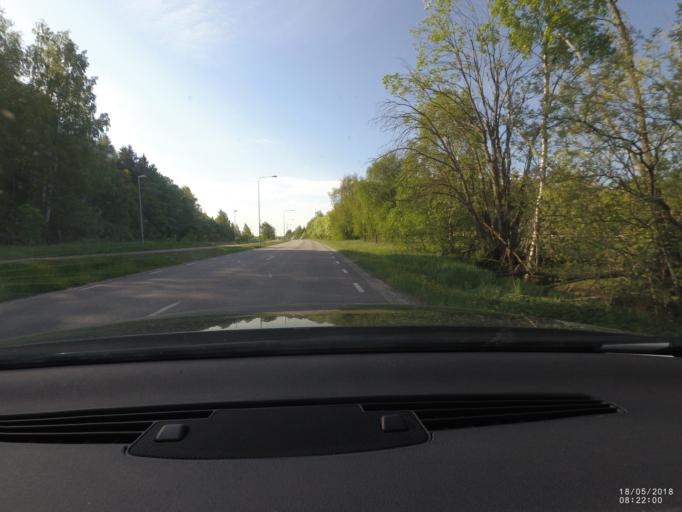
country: SE
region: Soedermanland
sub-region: Nykopings Kommun
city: Nykoping
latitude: 58.7349
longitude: 17.0058
